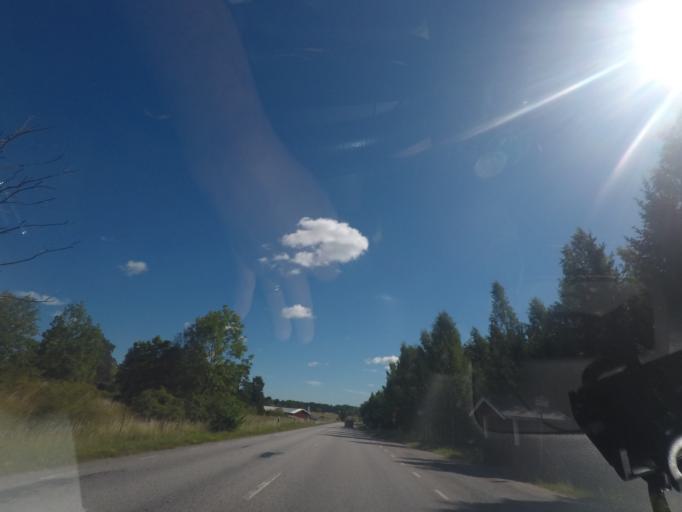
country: SE
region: Uppsala
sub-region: Uppsala Kommun
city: Alsike
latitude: 59.8555
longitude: 17.8334
